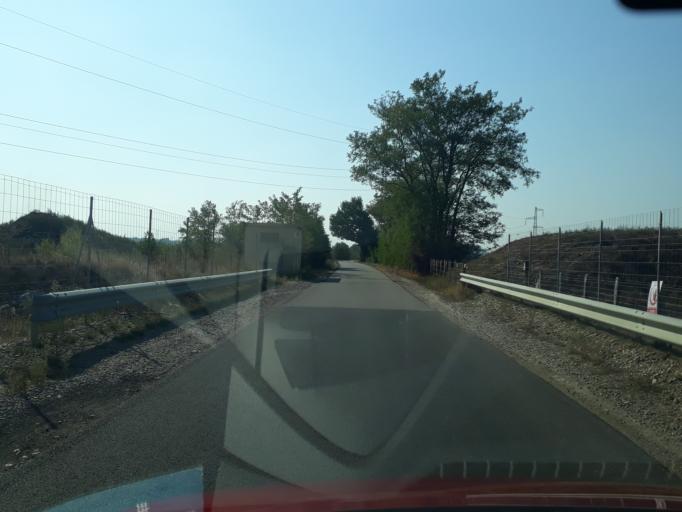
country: FR
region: Rhone-Alpes
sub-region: Departement du Rhone
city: Saint-Bonnet-de-Mure
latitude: 45.6786
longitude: 5.0121
